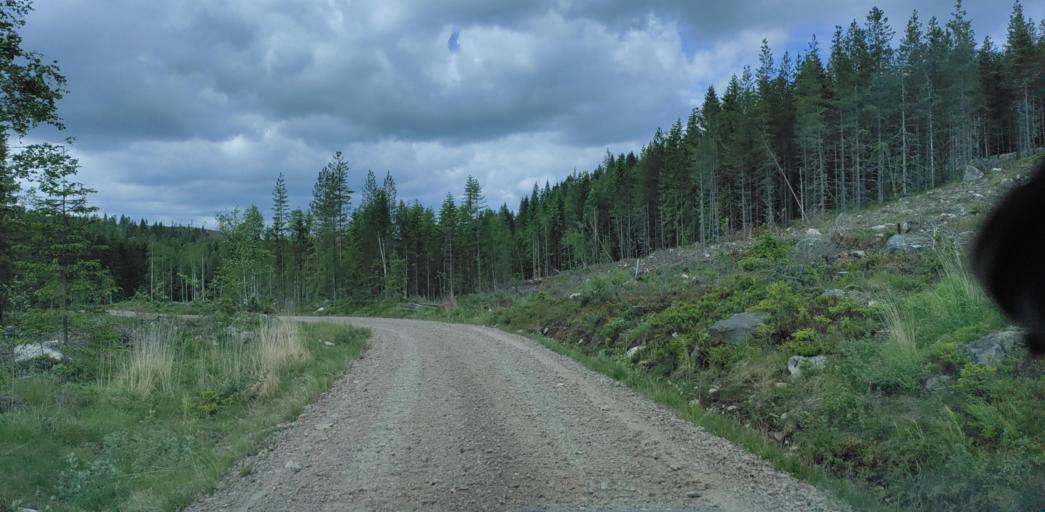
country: SE
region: Vaermland
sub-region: Munkfors Kommun
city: Munkfors
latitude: 59.9512
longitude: 13.4144
